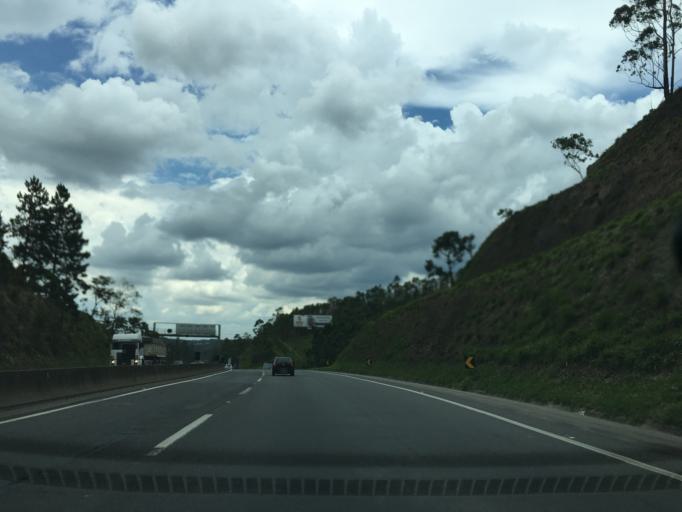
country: BR
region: Sao Paulo
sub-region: Mairipora
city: Mairipora
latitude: -23.2811
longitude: -46.5867
